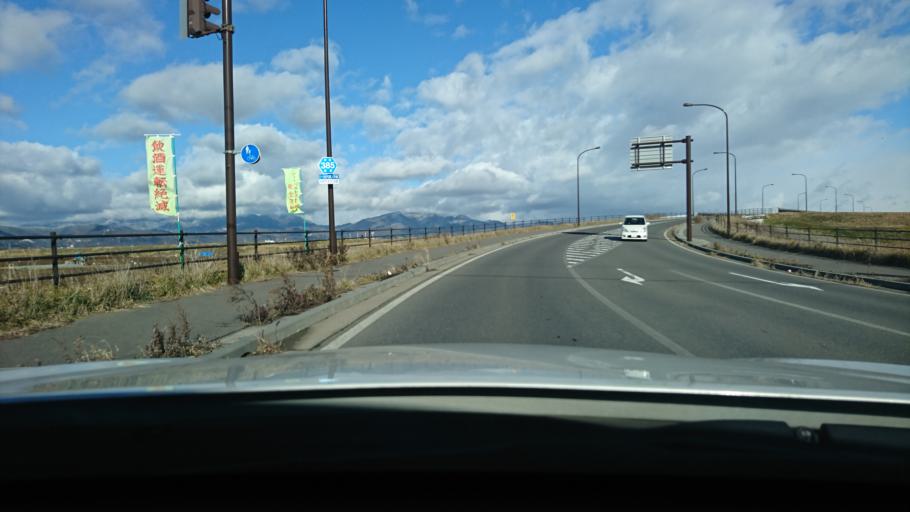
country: JP
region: Nagano
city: Nagano-shi
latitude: 36.5644
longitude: 138.1729
